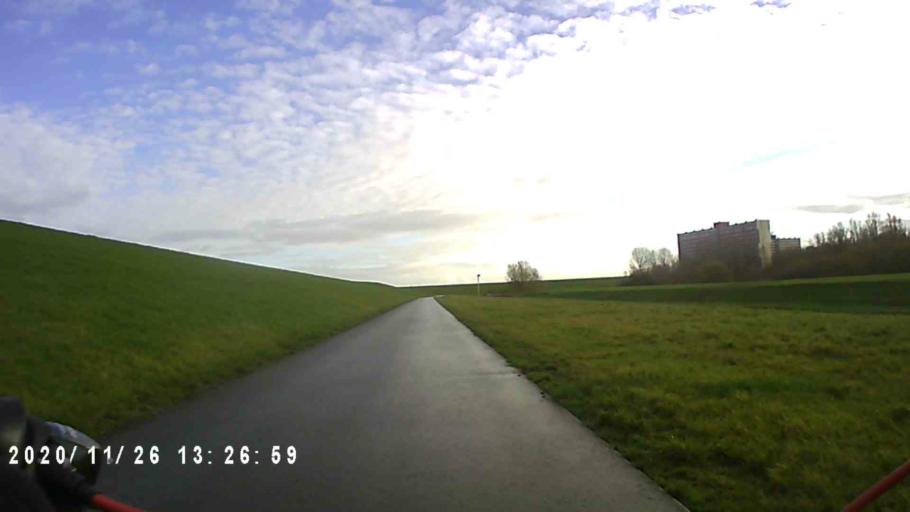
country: NL
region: Groningen
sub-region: Gemeente Delfzijl
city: Delfzijl
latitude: 53.3472
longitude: 6.9036
